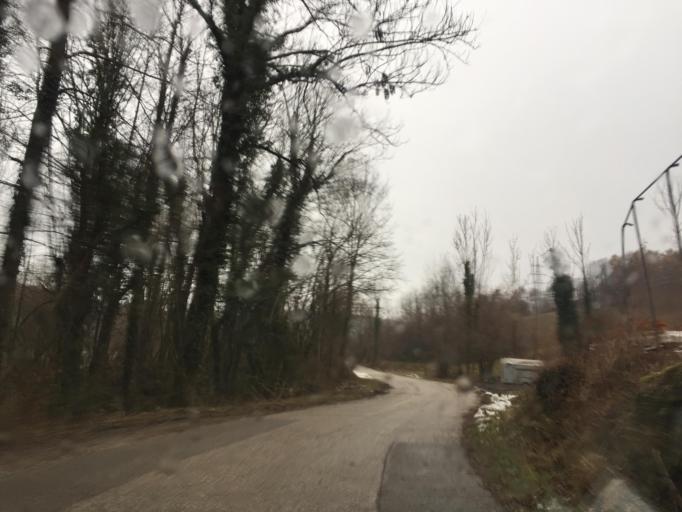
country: SI
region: Kanal
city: Kanal
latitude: 46.0707
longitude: 13.6657
